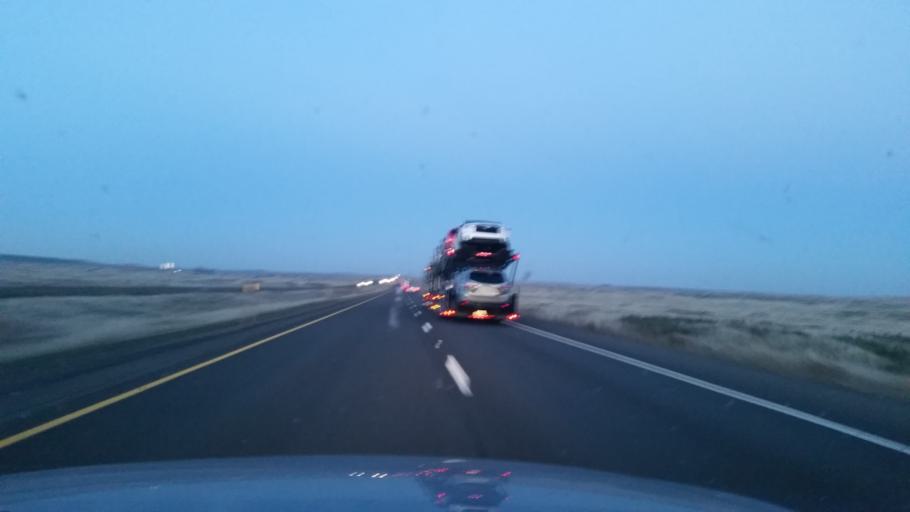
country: US
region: Washington
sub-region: Adams County
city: Ritzville
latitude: 47.1363
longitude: -118.3372
